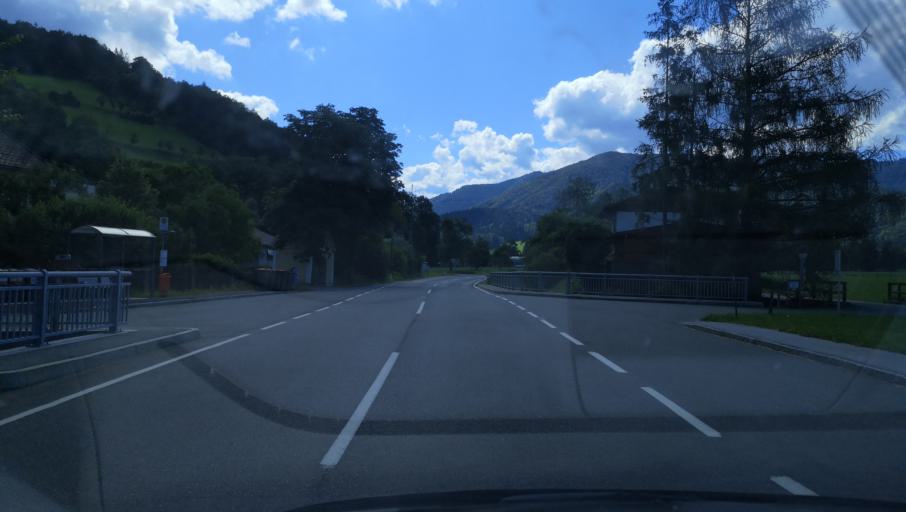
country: AT
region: Lower Austria
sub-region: Politischer Bezirk Scheibbs
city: Gresten
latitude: 47.9609
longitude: 15.0273
